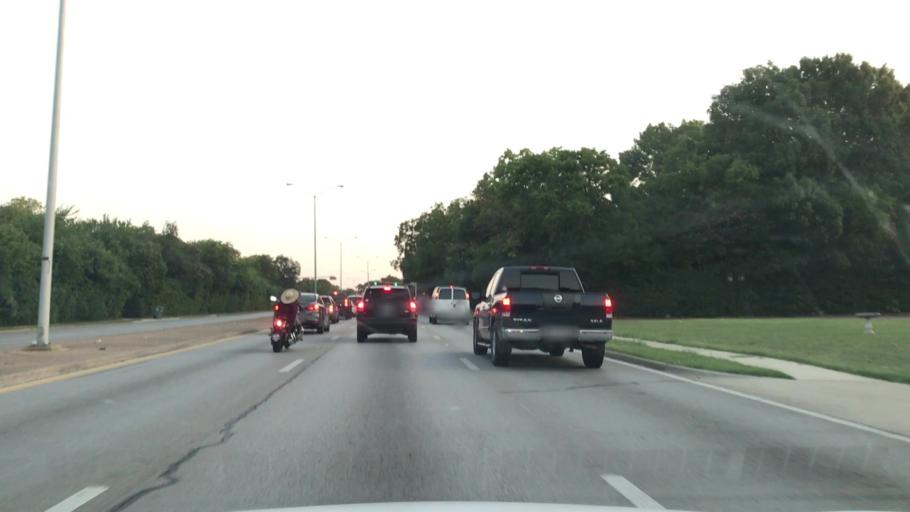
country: US
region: Texas
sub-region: Dallas County
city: Highland Park
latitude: 32.8268
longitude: -96.6973
